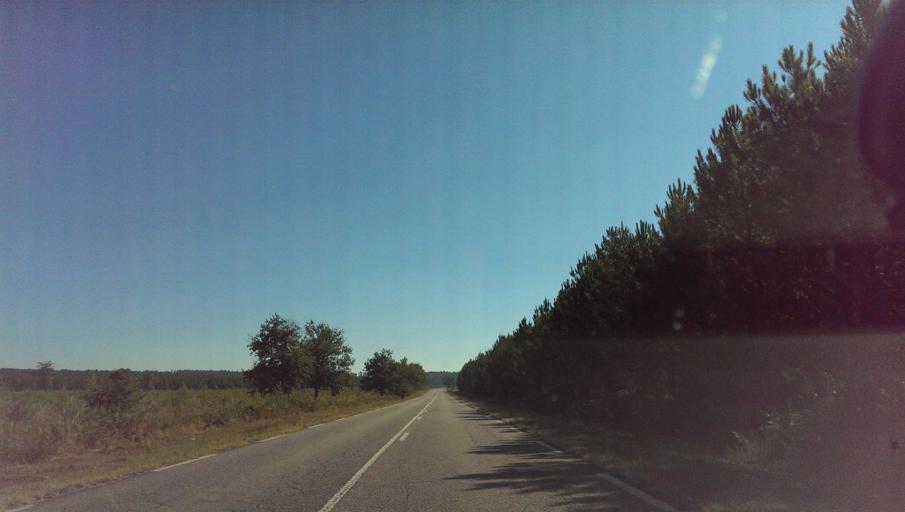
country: FR
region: Aquitaine
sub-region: Departement du Lot-et-Garonne
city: Barbaste
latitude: 44.2196
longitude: 0.2104
